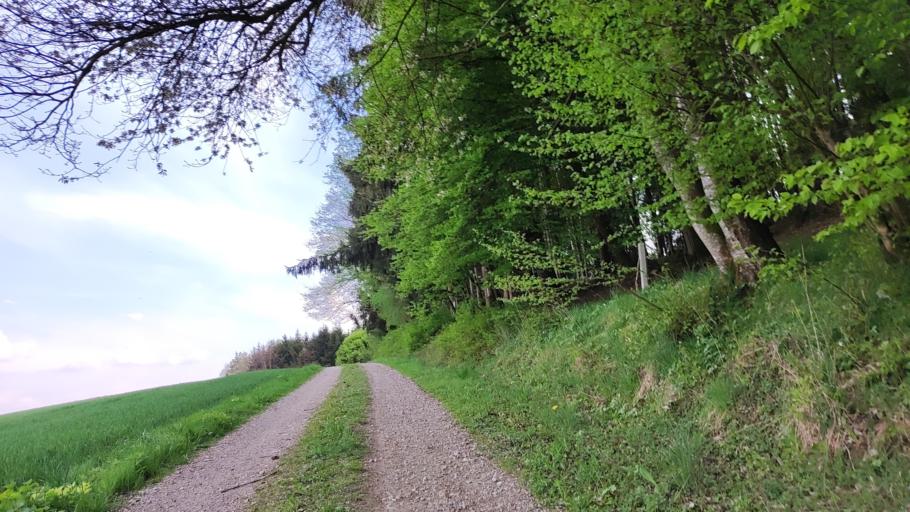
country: DE
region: Bavaria
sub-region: Swabia
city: Zusmarshausen
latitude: 48.3971
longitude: 10.5730
